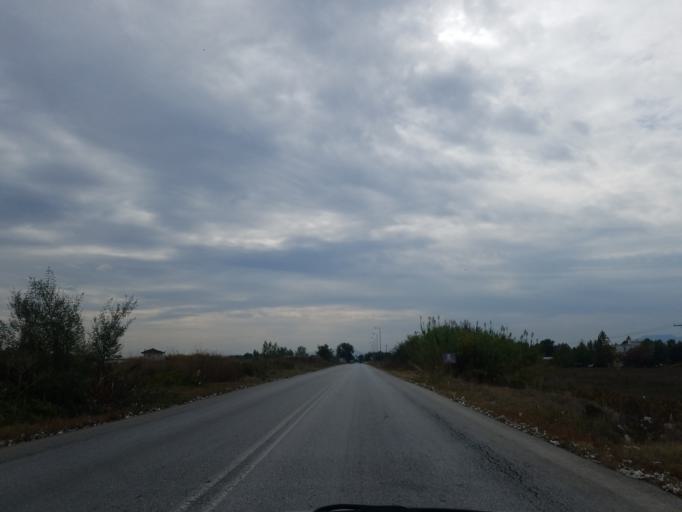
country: GR
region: Thessaly
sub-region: Nomos Kardhitsas
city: Sofades
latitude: 39.3356
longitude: 22.0850
